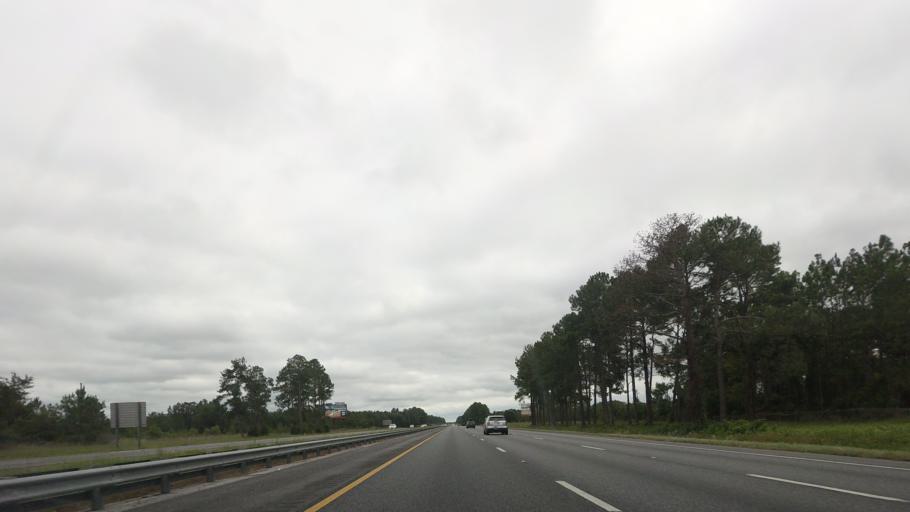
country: US
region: Florida
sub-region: Columbia County
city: Lake City
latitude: 30.1706
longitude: -82.6840
